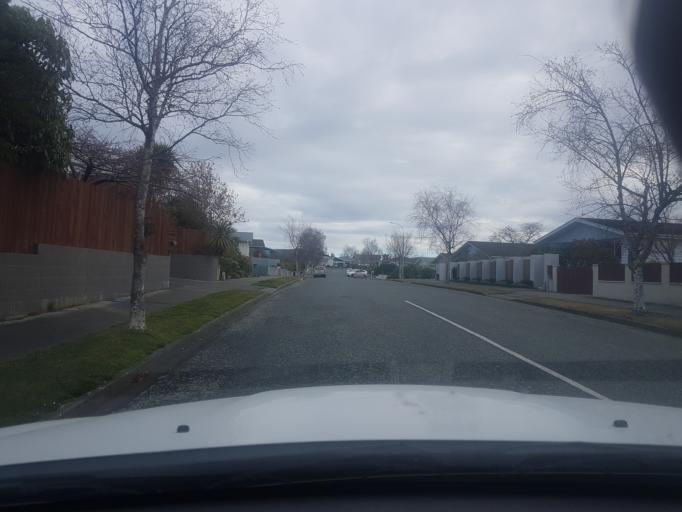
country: NZ
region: Canterbury
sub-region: Timaru District
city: Timaru
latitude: -44.3891
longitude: 171.2037
